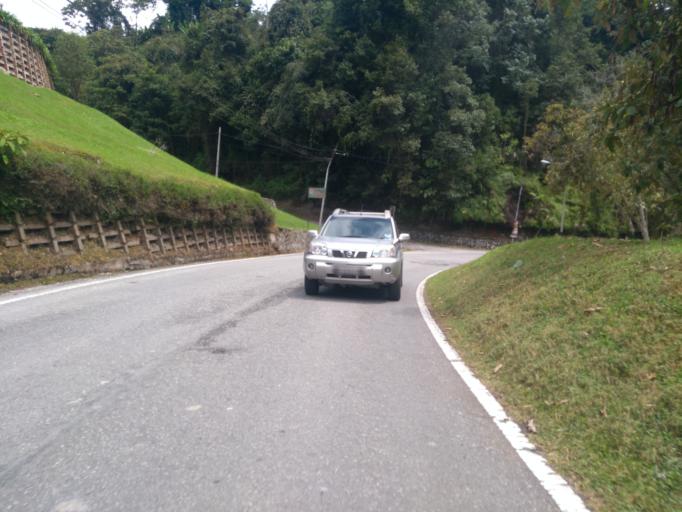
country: MY
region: Pahang
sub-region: Cameron Highlands
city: Tanah Rata
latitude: 4.4836
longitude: 101.3825
